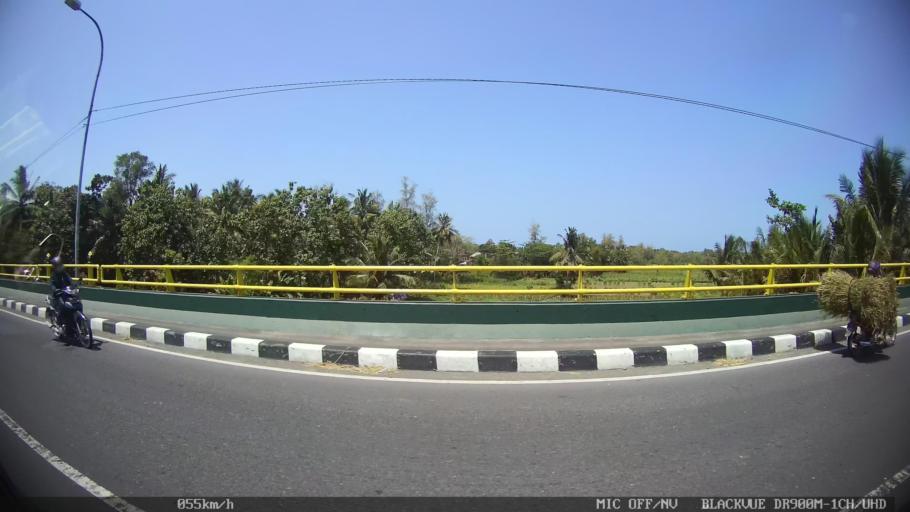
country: ID
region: Daerah Istimewa Yogyakarta
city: Srandakan
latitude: -7.9388
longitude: 110.2450
